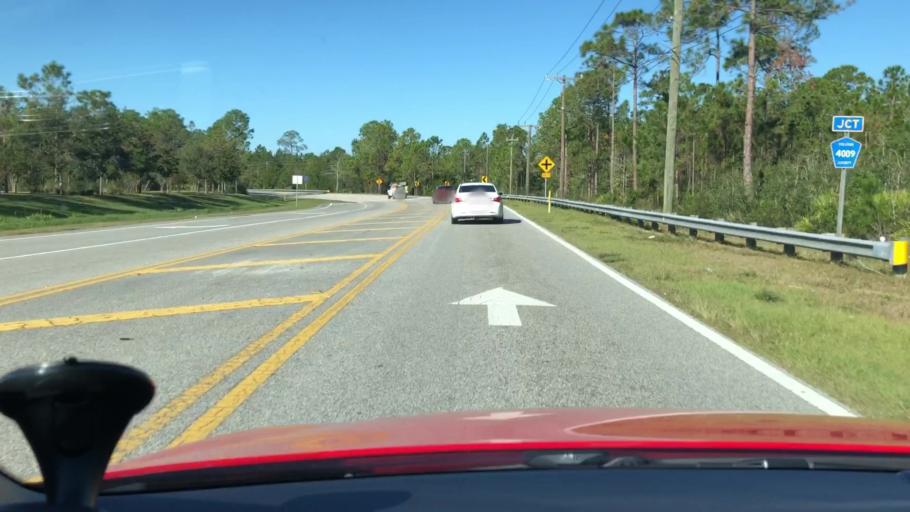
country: US
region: Florida
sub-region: Volusia County
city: Holly Hill
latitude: 29.2140
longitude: -81.0871
